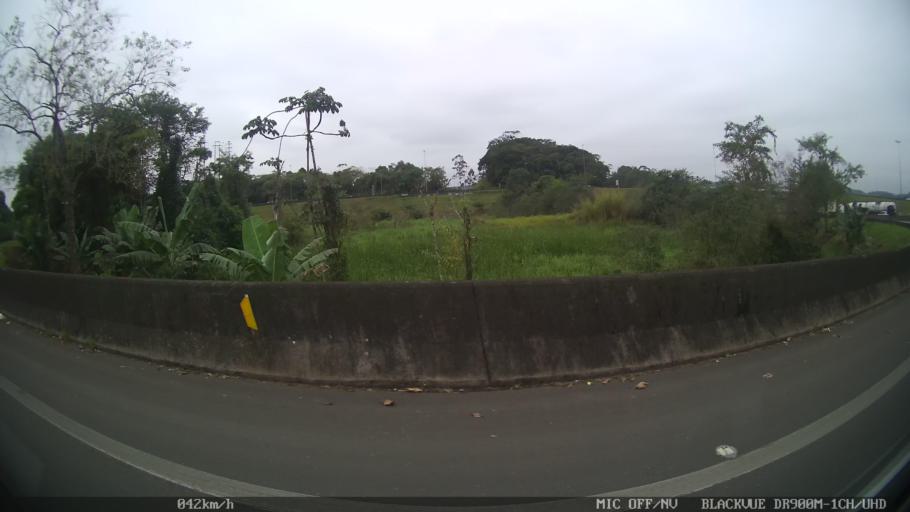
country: BR
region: Santa Catarina
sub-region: Joinville
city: Joinville
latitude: -26.3851
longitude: -48.8468
